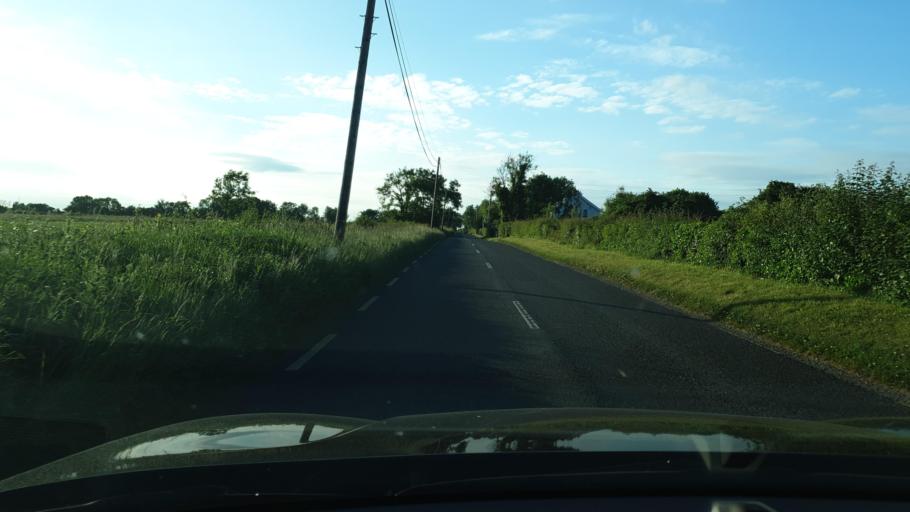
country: IE
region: Leinster
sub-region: An Mhi
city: Ratoath
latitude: 53.4924
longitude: -6.4372
